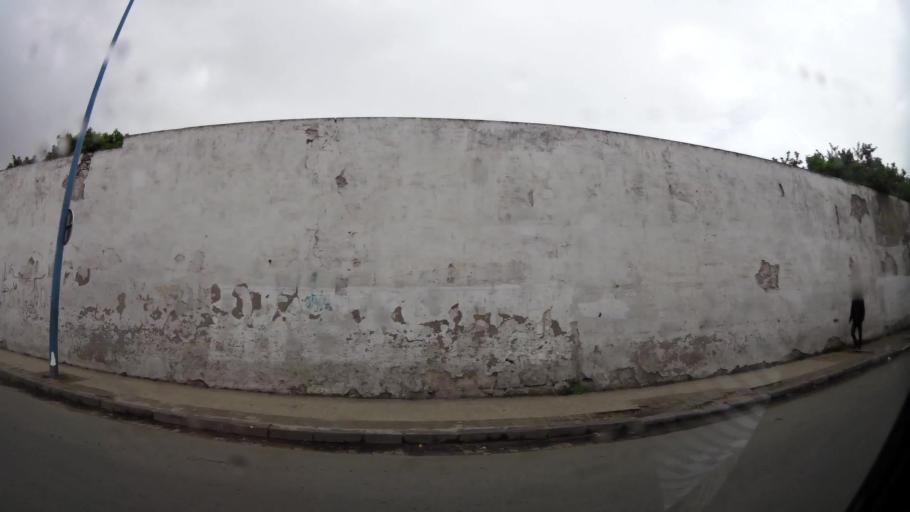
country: MA
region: Grand Casablanca
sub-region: Casablanca
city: Casablanca
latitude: 33.5768
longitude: -7.5965
